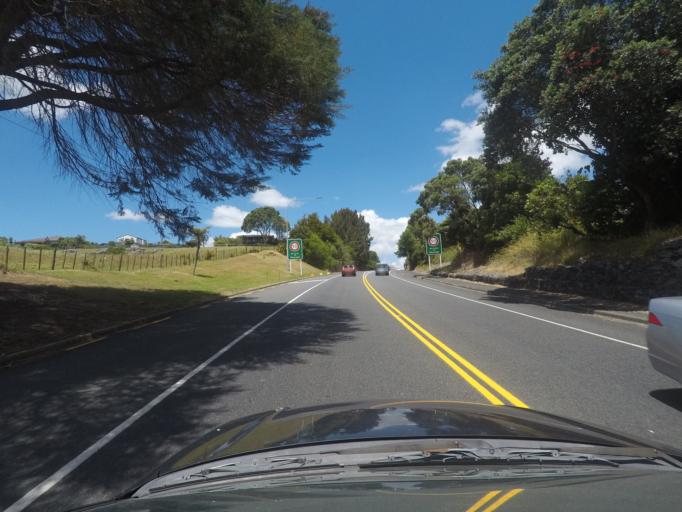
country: NZ
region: Northland
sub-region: Whangarei
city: Whangarei
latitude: -35.7430
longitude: 174.3657
